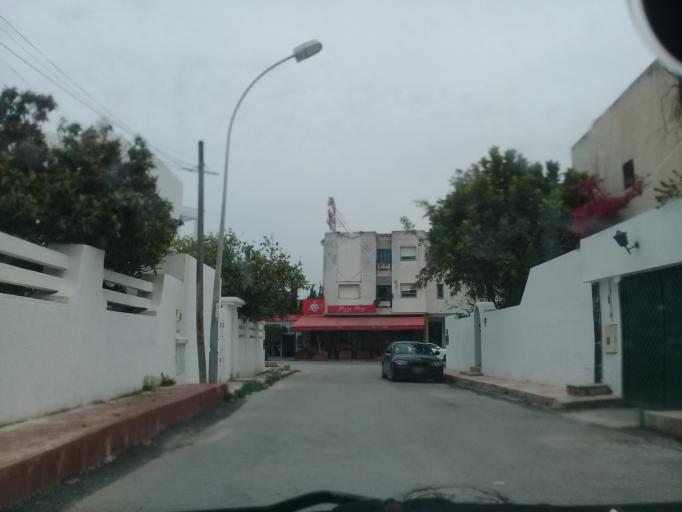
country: TN
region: Tunis
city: Tunis
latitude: 36.8426
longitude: 10.1580
